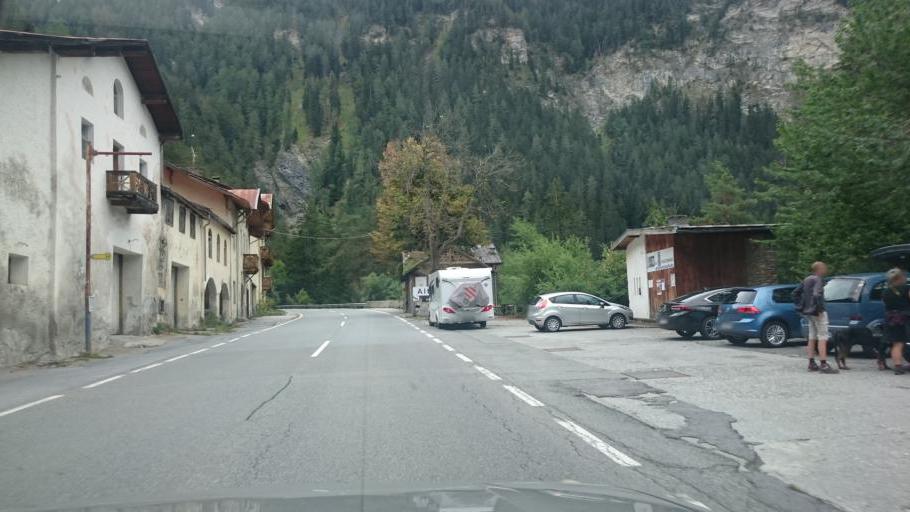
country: AT
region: Tyrol
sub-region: Politischer Bezirk Landeck
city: Nauders
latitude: 46.9301
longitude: 10.4894
